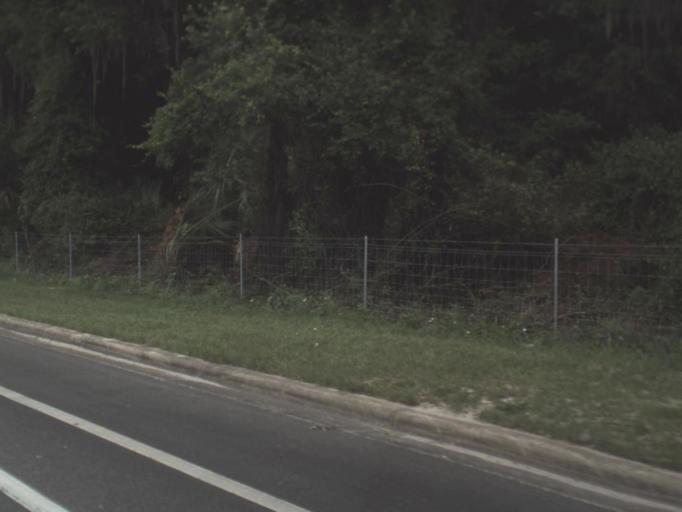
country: US
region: Florida
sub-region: Alachua County
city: Gainesville
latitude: 29.6176
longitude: -82.3335
